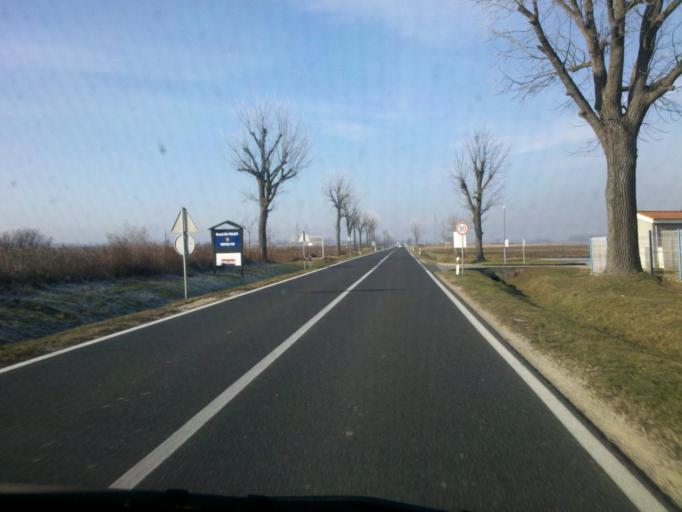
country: HR
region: Koprivnicko-Krizevacka
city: Kalinovac
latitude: 46.0135
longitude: 17.0953
